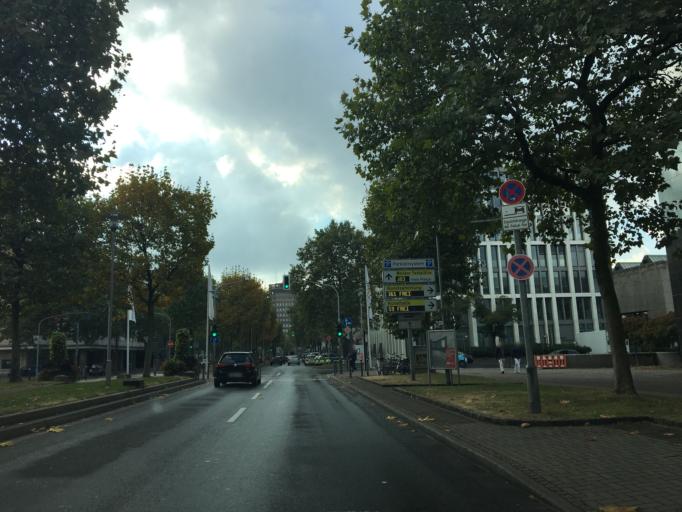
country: DE
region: North Rhine-Westphalia
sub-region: Regierungsbezirk Dusseldorf
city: Dusseldorf
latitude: 51.2283
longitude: 6.7768
